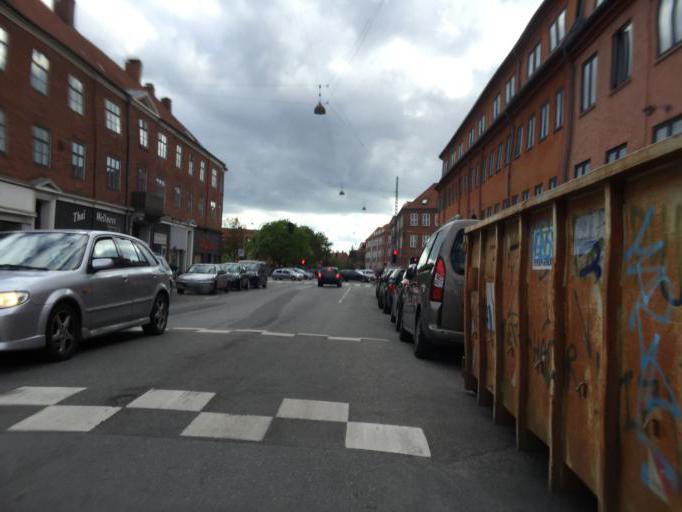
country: DK
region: Capital Region
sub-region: Frederiksberg Kommune
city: Frederiksberg
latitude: 55.6991
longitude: 12.5242
